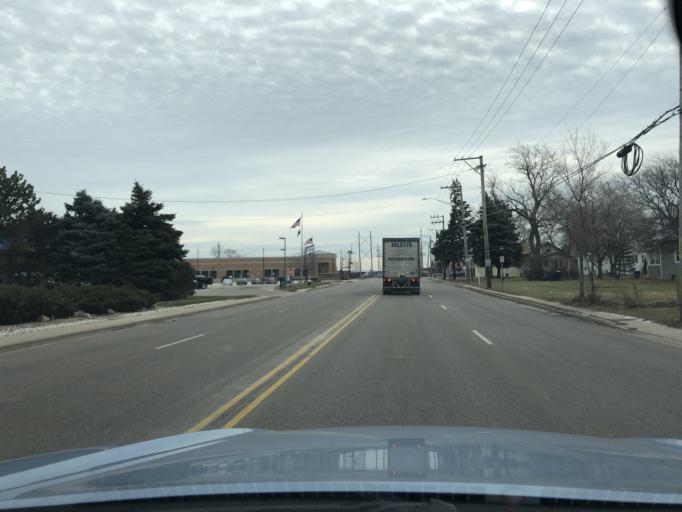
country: US
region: Illinois
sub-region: DuPage County
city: Bensenville
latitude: 41.9542
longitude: -87.9363
